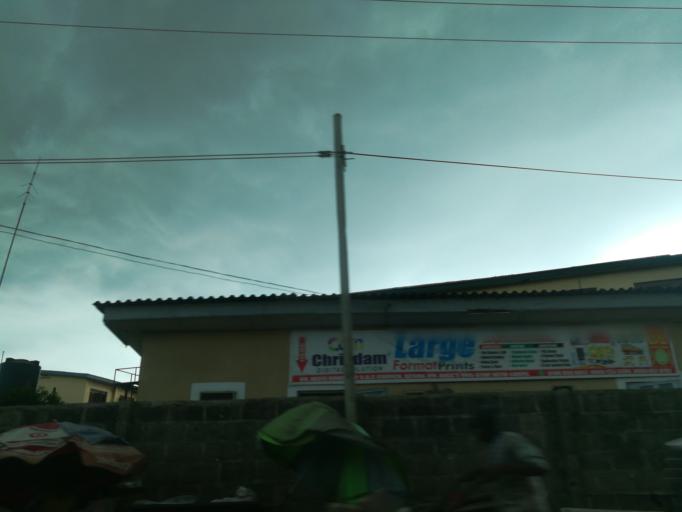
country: NG
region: Lagos
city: Ojota
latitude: 6.5997
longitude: 3.3809
